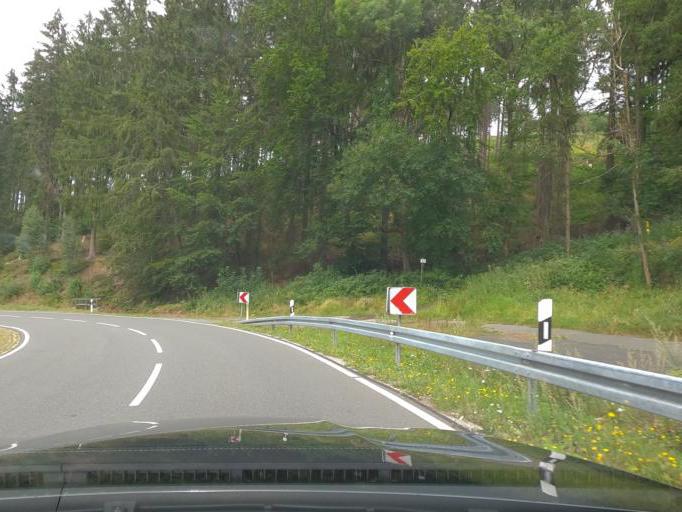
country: DE
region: Lower Saxony
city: Wildemann
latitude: 51.8607
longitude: 10.3197
